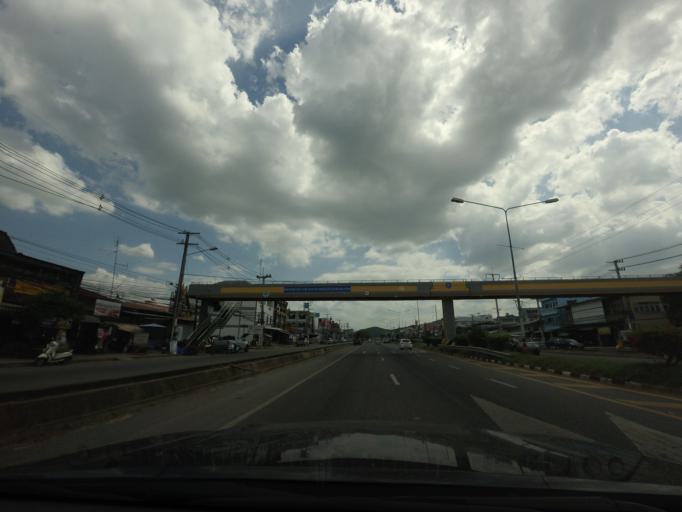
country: TH
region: Phetchabun
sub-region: Amphoe Bueng Sam Phan
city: Bueng Sam Phan
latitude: 15.7878
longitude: 101.0064
